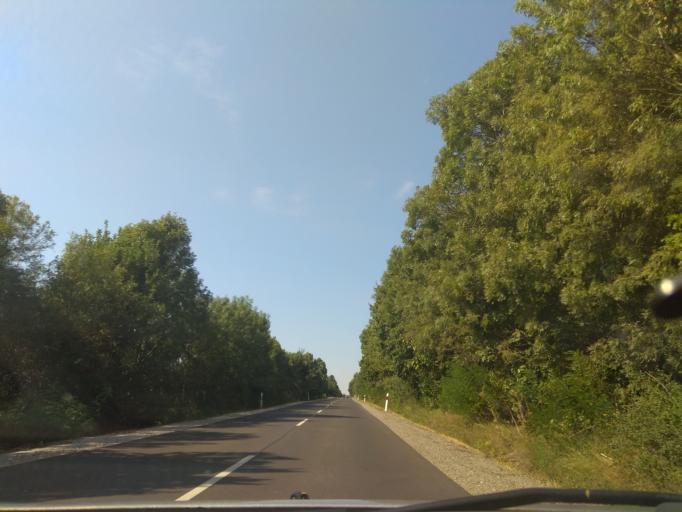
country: HU
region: Borsod-Abauj-Zemplen
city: Harsany
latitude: 47.9375
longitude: 20.7386
